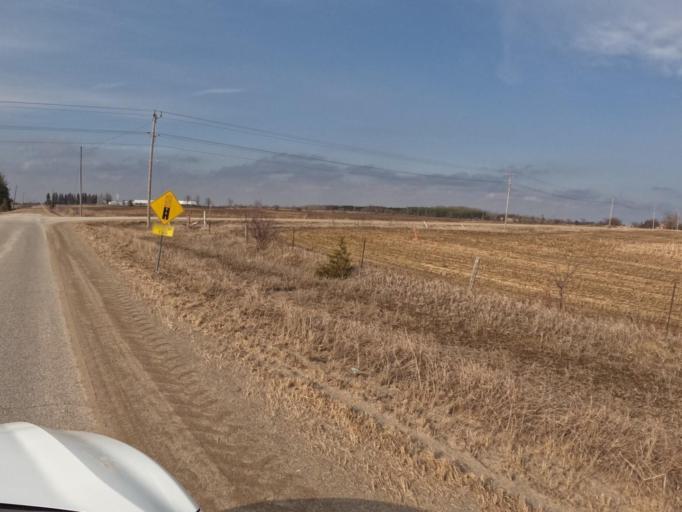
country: CA
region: Ontario
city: Orangeville
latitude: 43.9074
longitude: -80.2865
